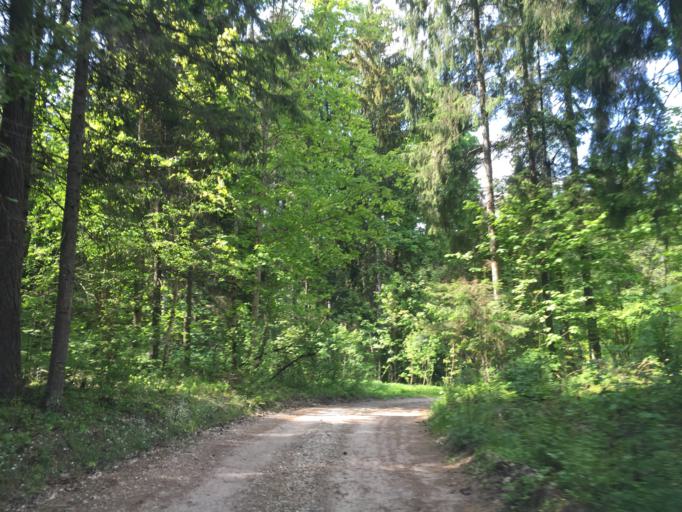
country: LV
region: Baldone
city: Baldone
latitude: 56.7820
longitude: 24.4214
